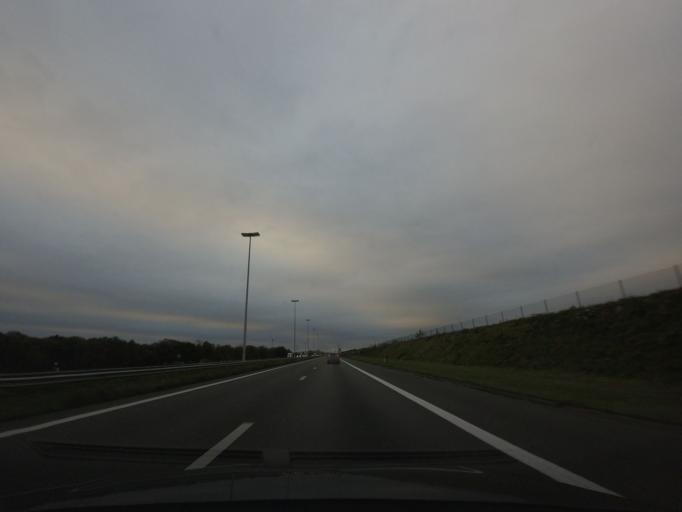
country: BE
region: Flanders
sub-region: Provincie Antwerpen
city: Hoogstraten
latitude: 51.4315
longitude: 4.7112
